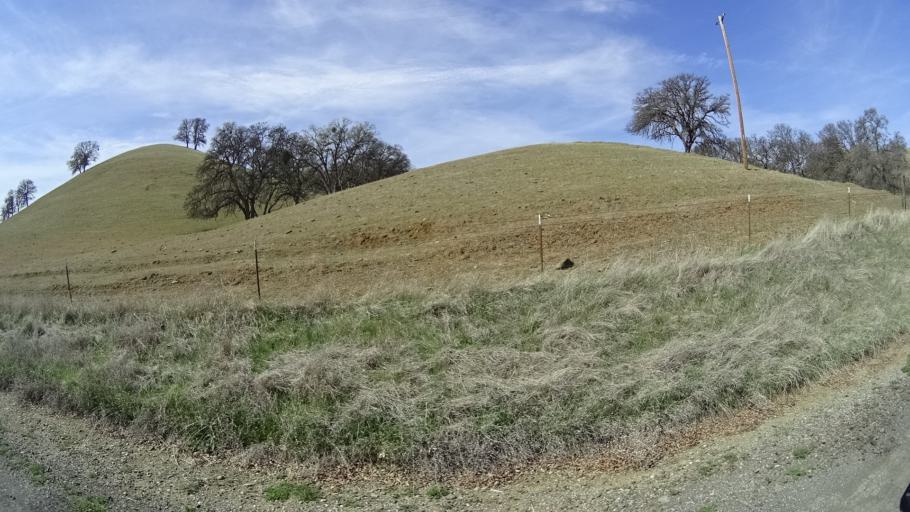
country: US
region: California
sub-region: Glenn County
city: Willows
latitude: 39.4880
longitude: -122.4532
